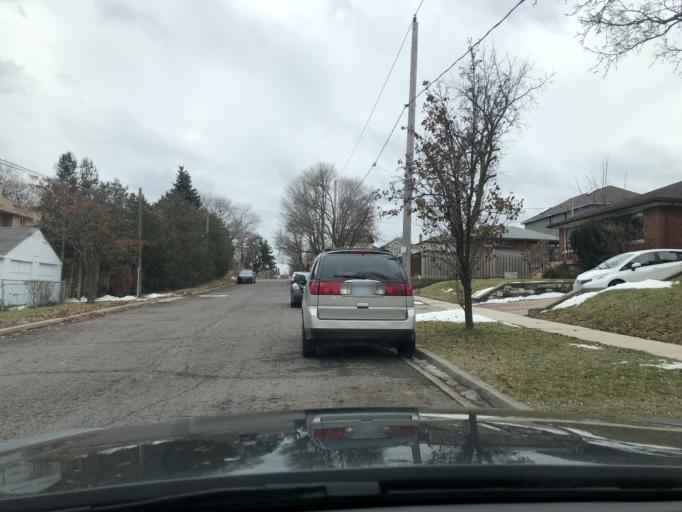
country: CA
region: Ontario
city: Etobicoke
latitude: 43.6997
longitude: -79.5287
